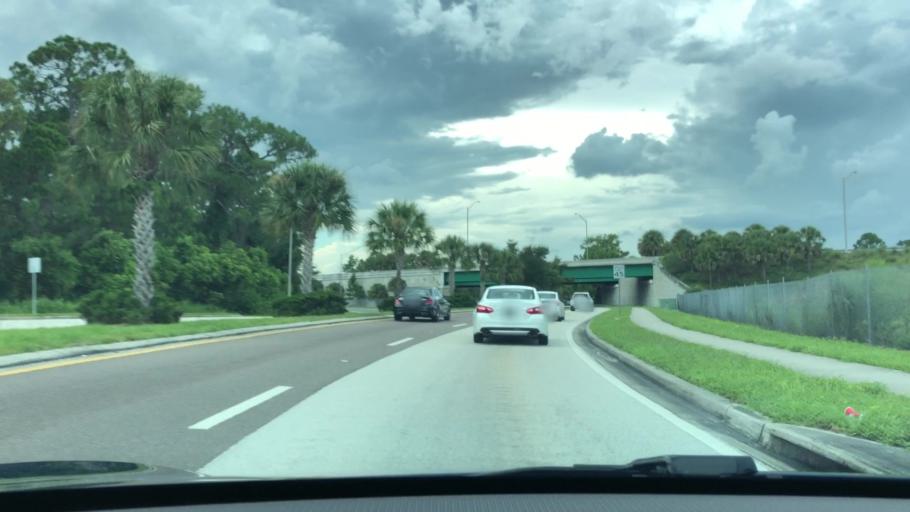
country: US
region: Florida
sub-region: Seminole County
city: Sanford
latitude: 28.7702
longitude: -81.2828
